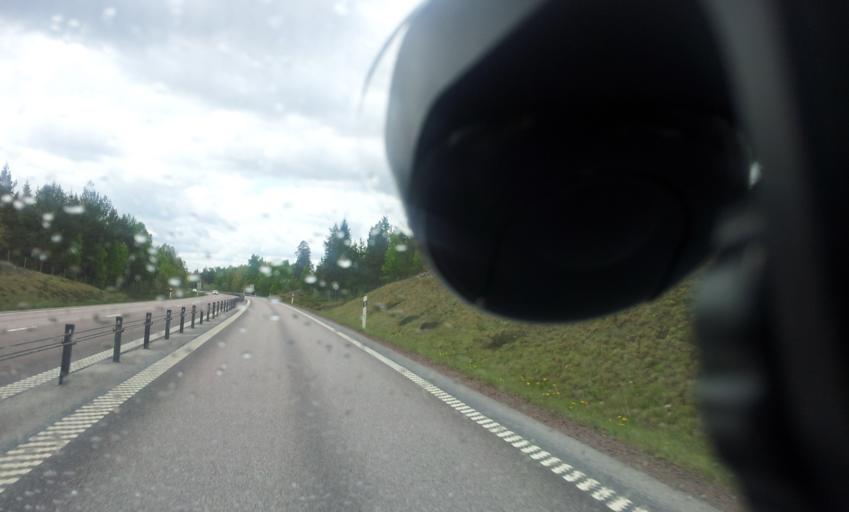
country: SE
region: Kalmar
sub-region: Oskarshamns Kommun
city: Oskarshamn
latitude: 57.2188
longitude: 16.4351
